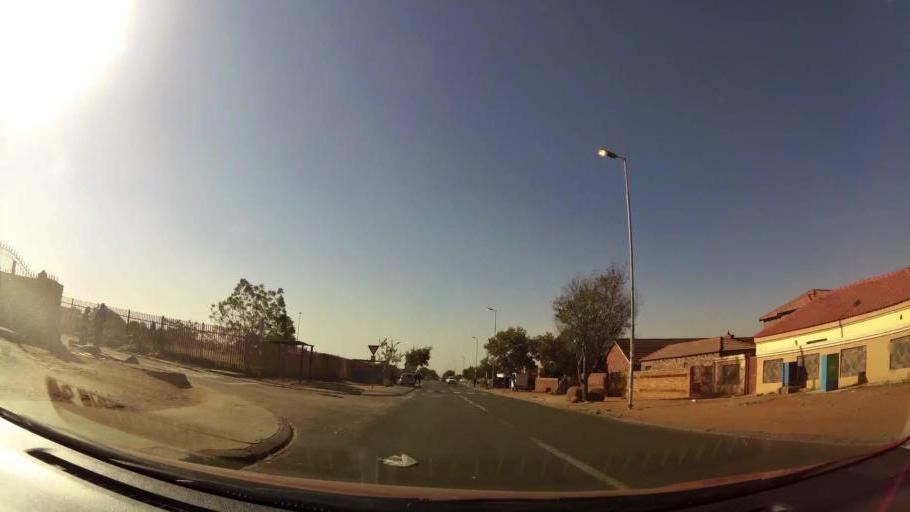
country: ZA
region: Gauteng
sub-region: City of Tshwane Metropolitan Municipality
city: Mabopane
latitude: -25.5341
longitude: 28.1016
